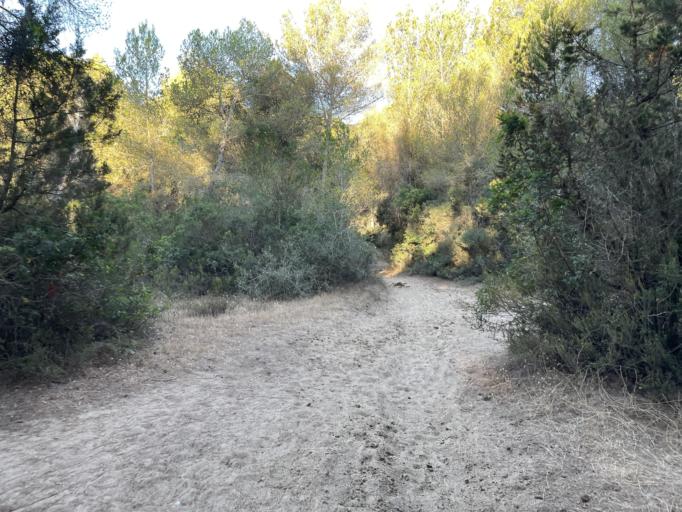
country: ES
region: Balearic Islands
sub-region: Illes Balears
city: Capdepera
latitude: 39.7150
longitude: 3.4533
